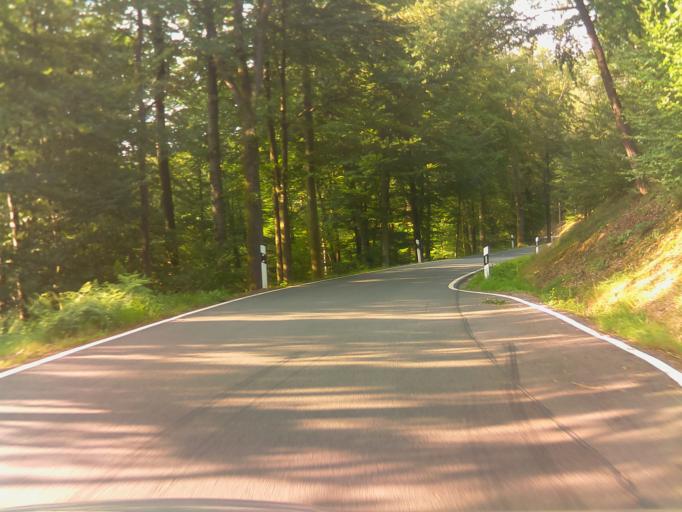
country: DE
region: Hesse
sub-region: Regierungsbezirk Darmstadt
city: Hesseneck
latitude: 49.5637
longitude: 9.0982
